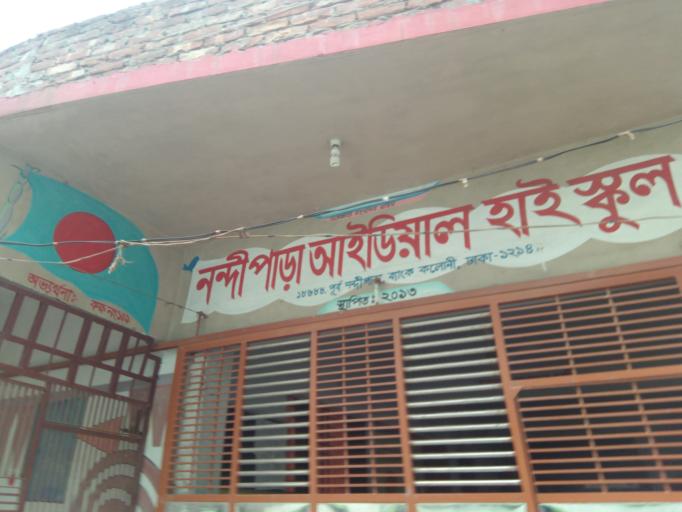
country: BD
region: Dhaka
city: Paltan
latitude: 23.7451
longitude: 90.4559
